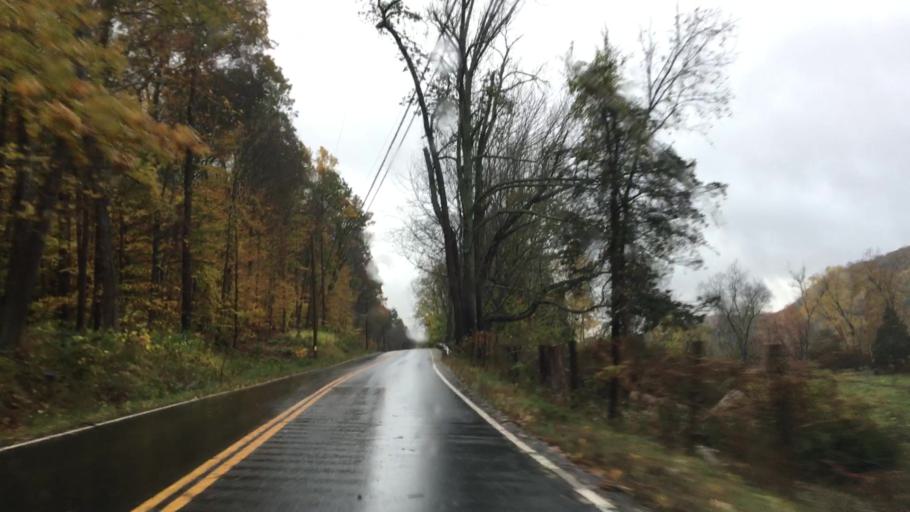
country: US
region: Connecticut
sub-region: New Haven County
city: Oxford
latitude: 41.4423
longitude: -73.1558
